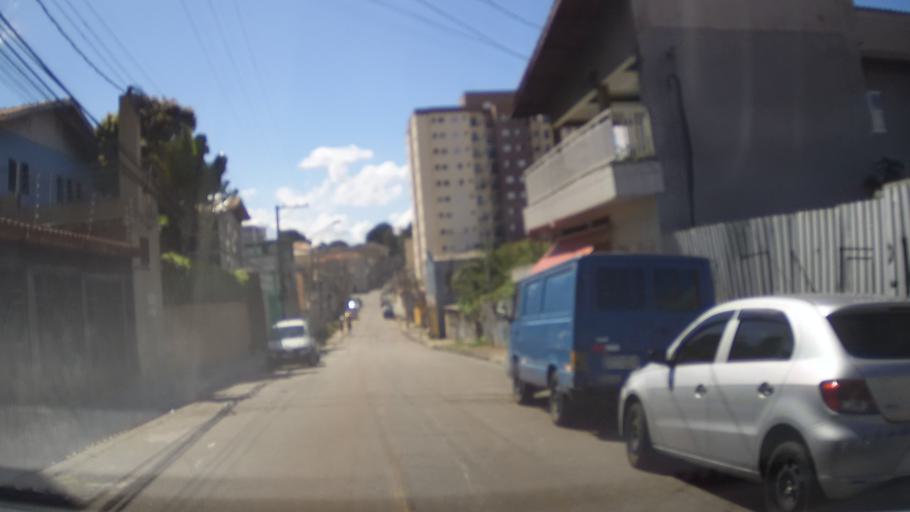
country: BR
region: Sao Paulo
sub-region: Guarulhos
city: Guarulhos
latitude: -23.4528
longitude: -46.5457
